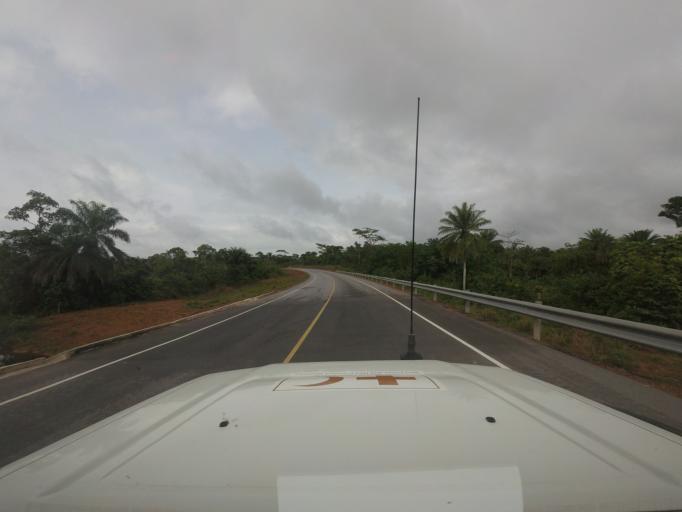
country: LR
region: Bong
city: Gbarnga
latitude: 7.0363
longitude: -9.2664
